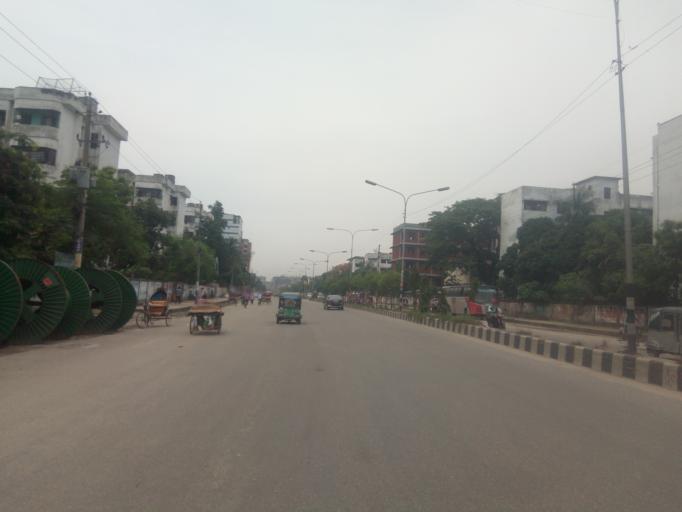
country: BD
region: Dhaka
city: Azimpur
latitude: 23.7856
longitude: 90.3539
